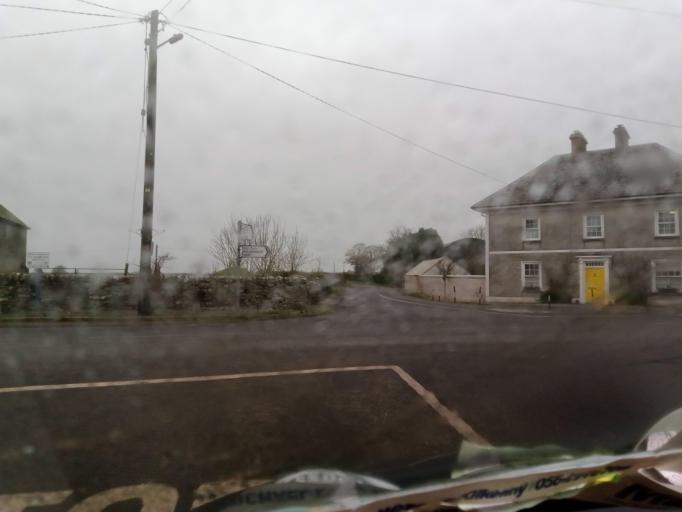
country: IE
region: Munster
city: Thurles
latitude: 52.5639
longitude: -7.7674
